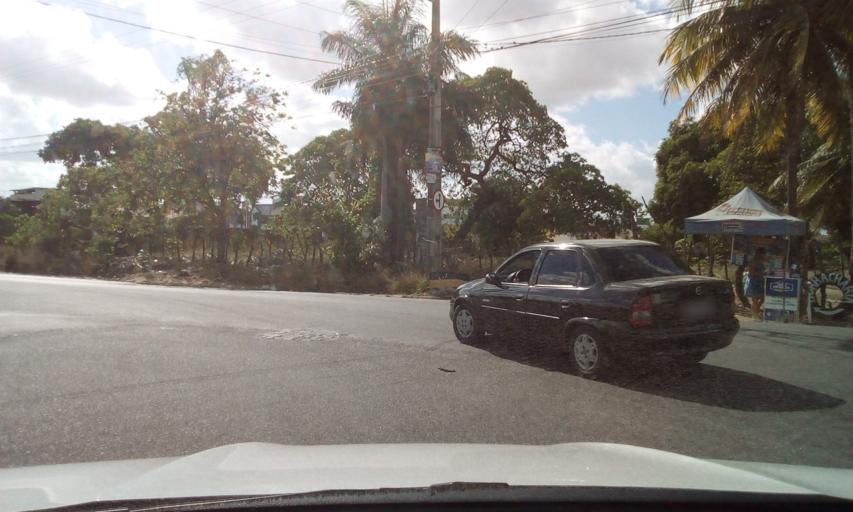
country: BR
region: Paraiba
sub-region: Bayeux
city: Bayeux
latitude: -7.1765
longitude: -34.9128
